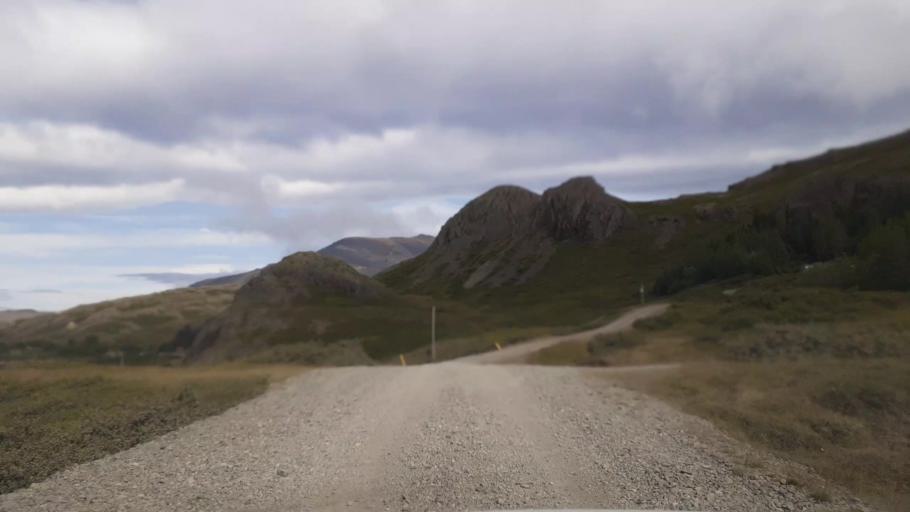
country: IS
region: East
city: Hoefn
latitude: 64.4293
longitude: -14.8863
